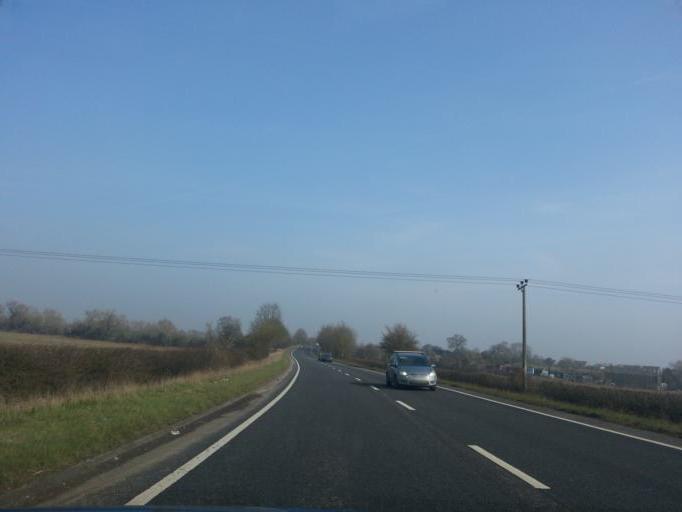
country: GB
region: England
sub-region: Oxfordshire
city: Shrivenham
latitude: 51.5924
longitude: -1.6719
